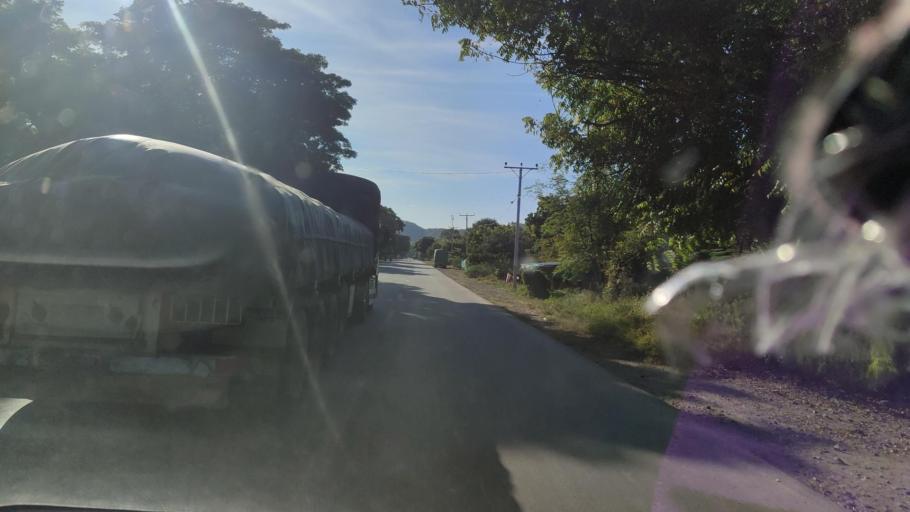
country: MM
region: Mandalay
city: Yamethin
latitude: 20.7537
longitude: 96.2474
